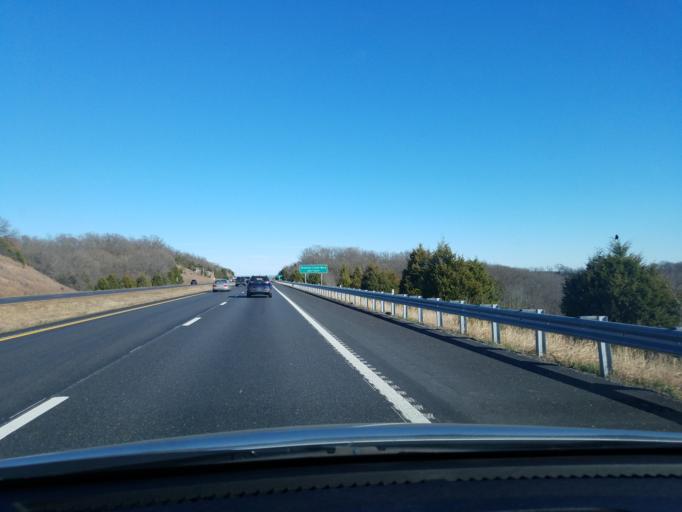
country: US
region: Missouri
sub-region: Taney County
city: Hollister
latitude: 36.5820
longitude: -93.2378
